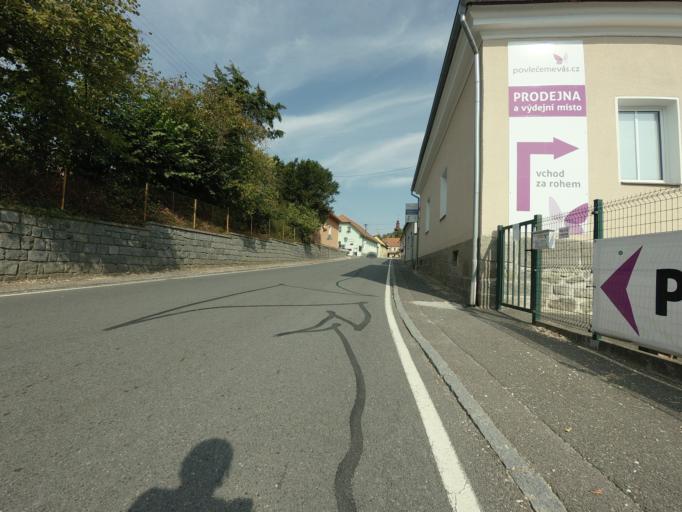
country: CZ
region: Central Bohemia
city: Petrovice
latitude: 49.5526
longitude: 14.3401
